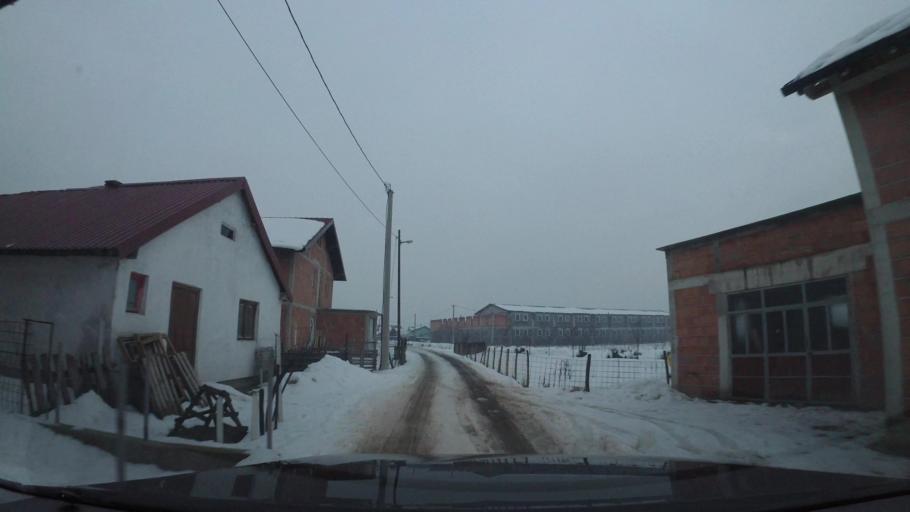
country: BA
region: Federation of Bosnia and Herzegovina
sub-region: Kanton Sarajevo
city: Sarajevo
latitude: 43.8524
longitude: 18.2895
